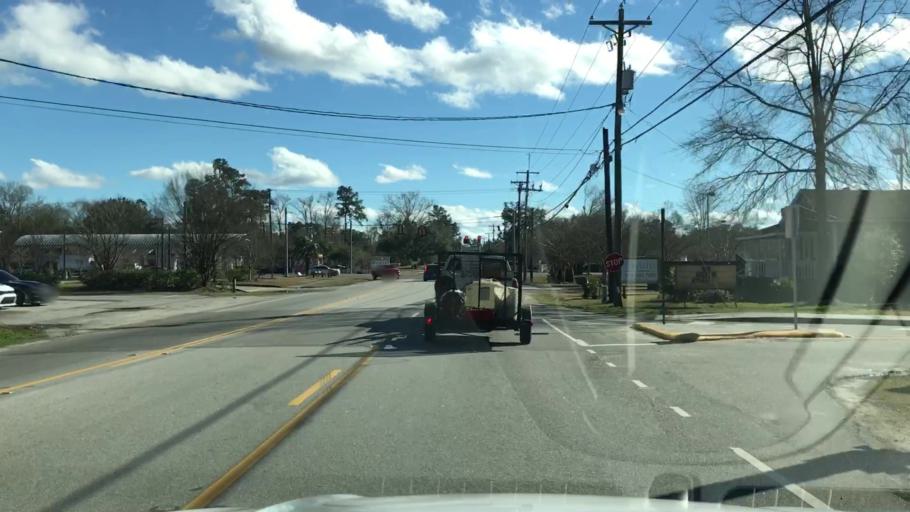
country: US
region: South Carolina
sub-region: Dorchester County
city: Summerville
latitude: 33.0130
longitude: -80.2382
